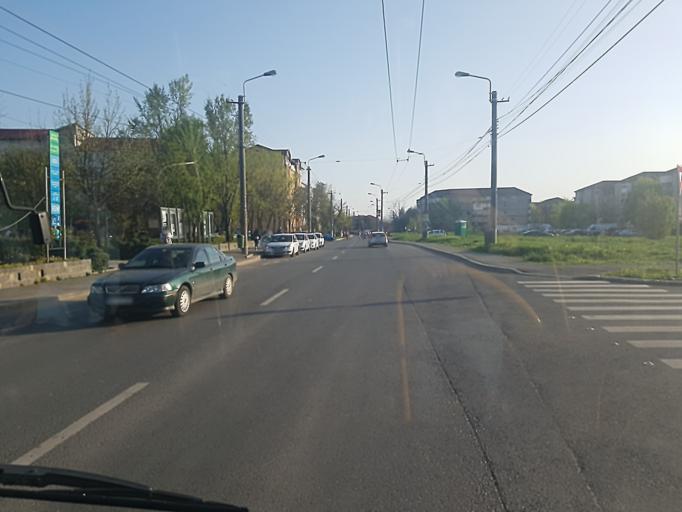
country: RO
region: Timis
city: Timisoara
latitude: 45.7343
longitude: 21.2488
